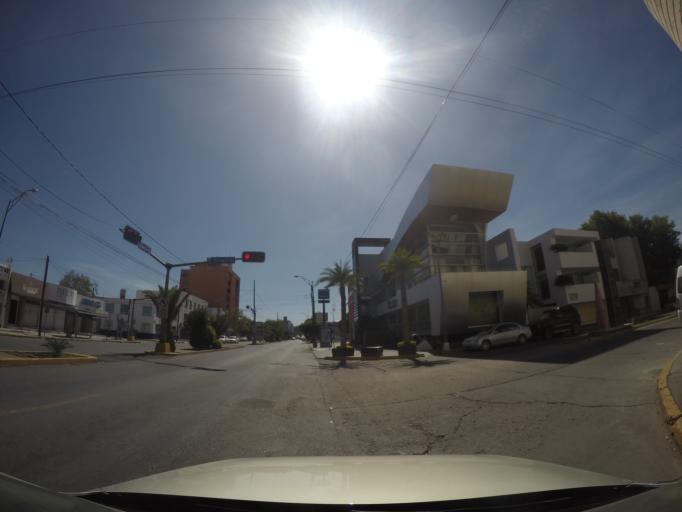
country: MX
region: San Luis Potosi
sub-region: San Luis Potosi
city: San Luis Potosi
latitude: 22.1489
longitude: -101.0106
